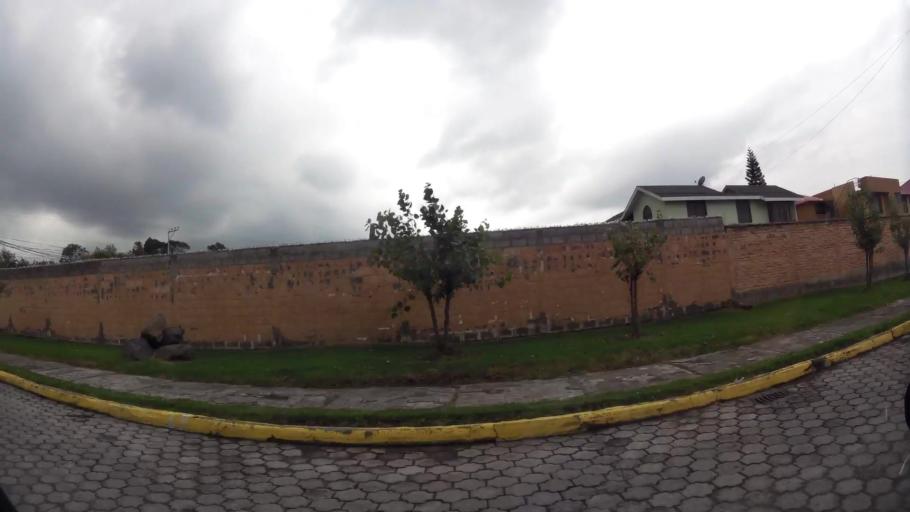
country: EC
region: Pichincha
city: Sangolqui
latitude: -0.3199
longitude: -78.4677
